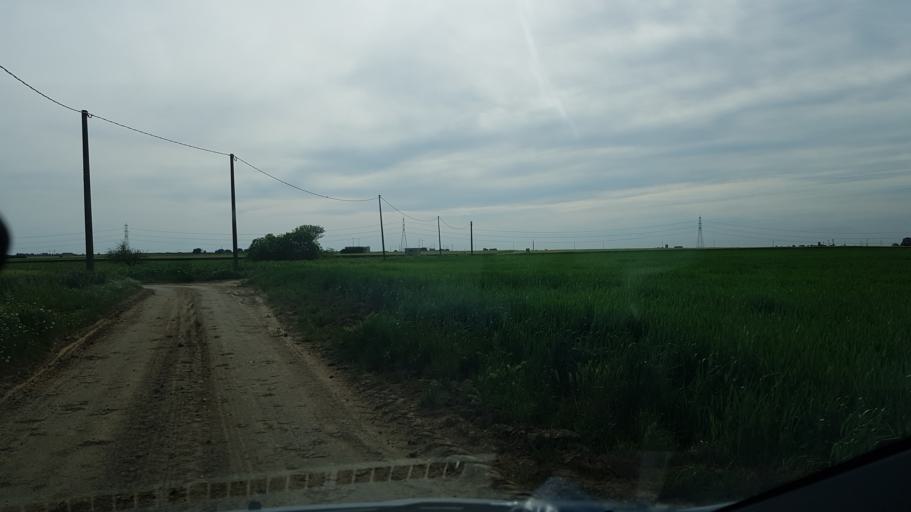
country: IT
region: Apulia
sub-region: Provincia di Brindisi
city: Tuturano
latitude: 40.5772
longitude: 17.9217
